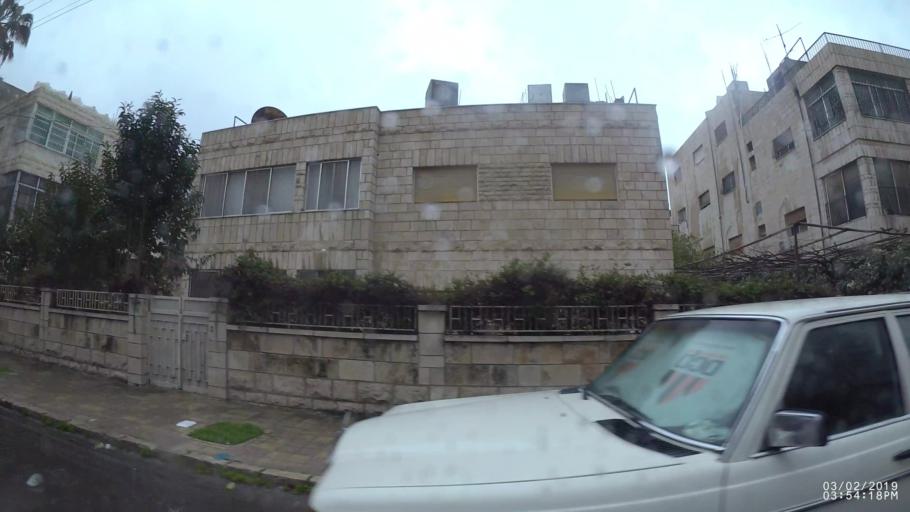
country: JO
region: Amman
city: Amman
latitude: 31.9726
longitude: 35.9159
